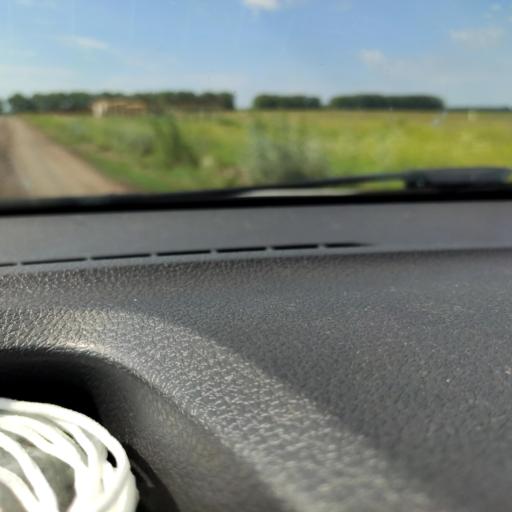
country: RU
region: Bashkortostan
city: Mikhaylovka
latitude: 54.8251
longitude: 55.7619
